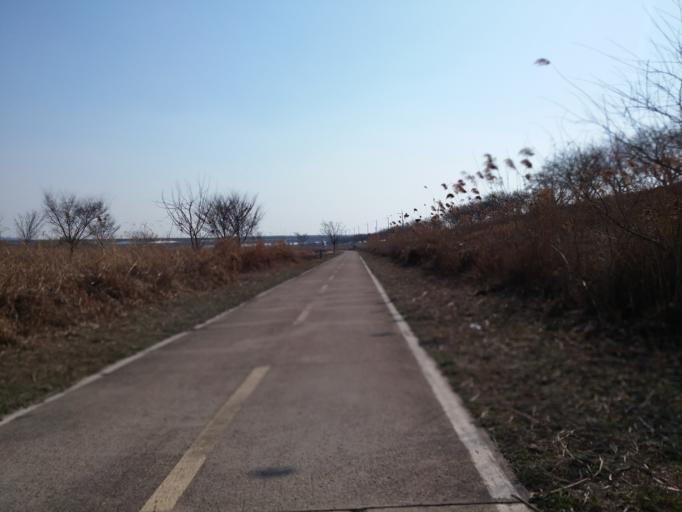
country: KR
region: Chungcheongbuk-do
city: Cheongju-si
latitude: 36.6185
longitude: 127.3455
